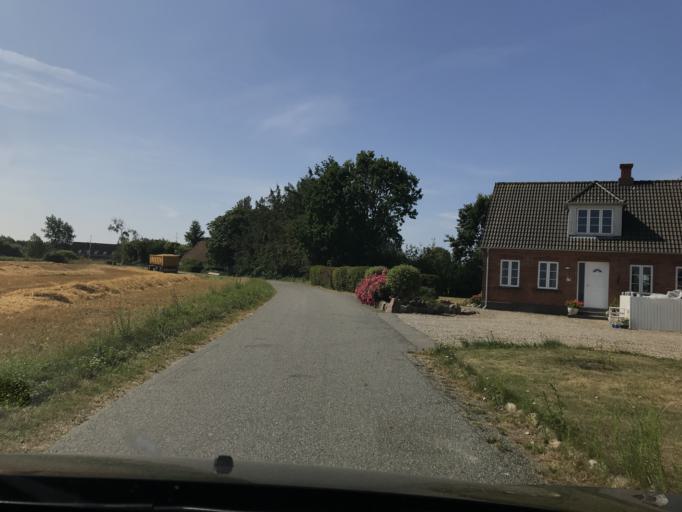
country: DK
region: South Denmark
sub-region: AEro Kommune
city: AEroskobing
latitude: 54.9336
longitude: 10.2818
